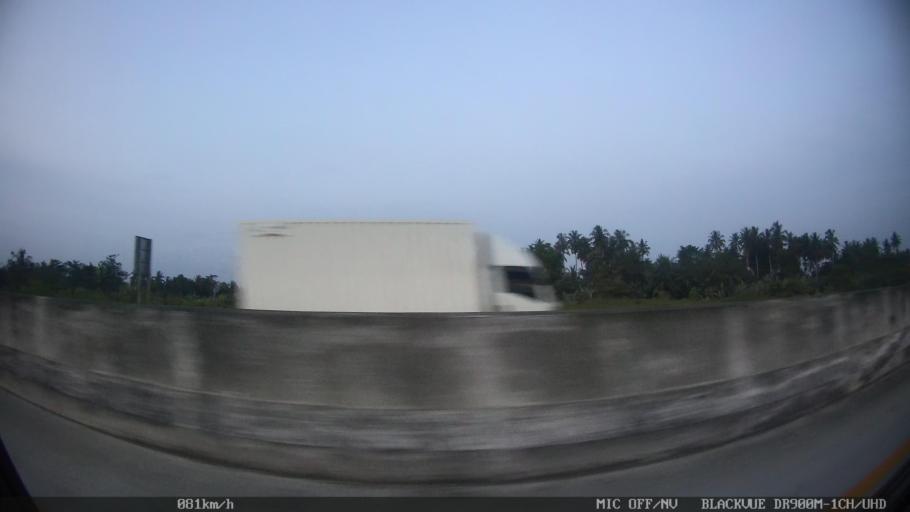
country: ID
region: Lampung
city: Sidorejo
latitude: -5.6474
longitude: 105.5792
